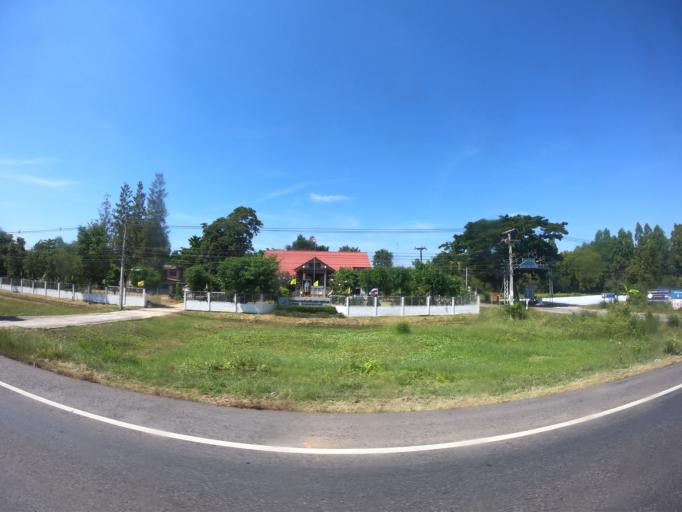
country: TH
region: Khon Kaen
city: Phon
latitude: 15.8849
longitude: 102.6416
